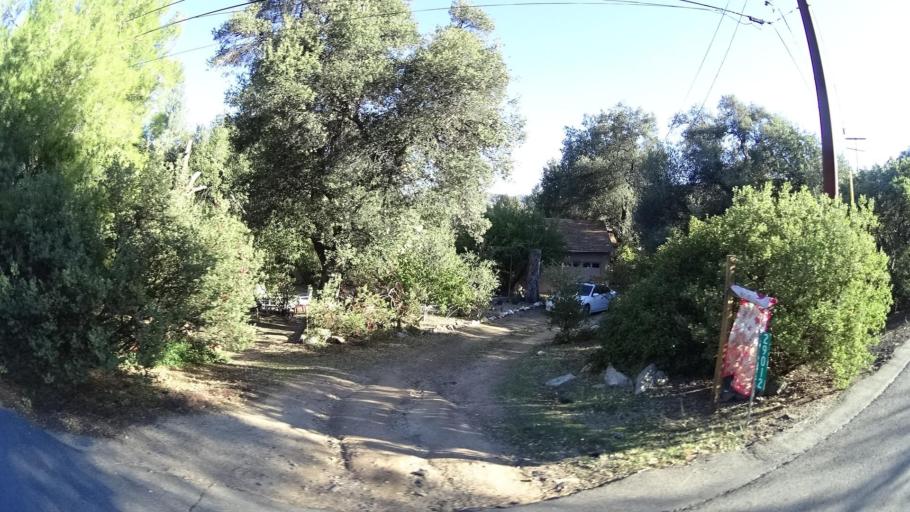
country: US
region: California
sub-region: San Diego County
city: Pine Valley
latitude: 32.8188
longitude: -116.5272
